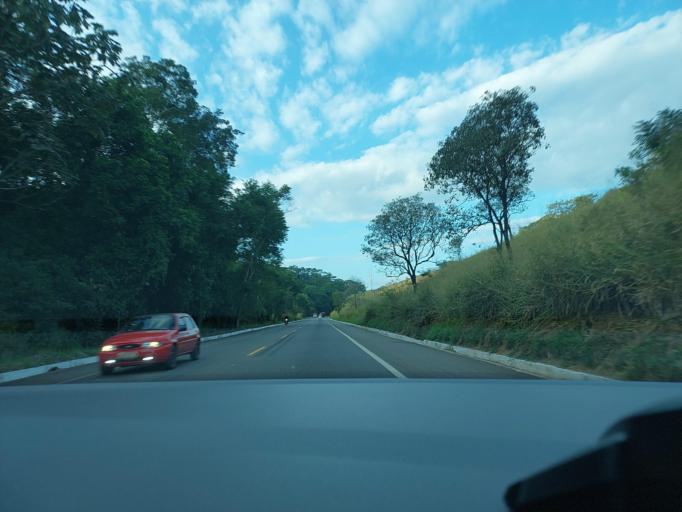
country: BR
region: Minas Gerais
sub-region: Muriae
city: Muriae
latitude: -21.1309
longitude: -42.2927
